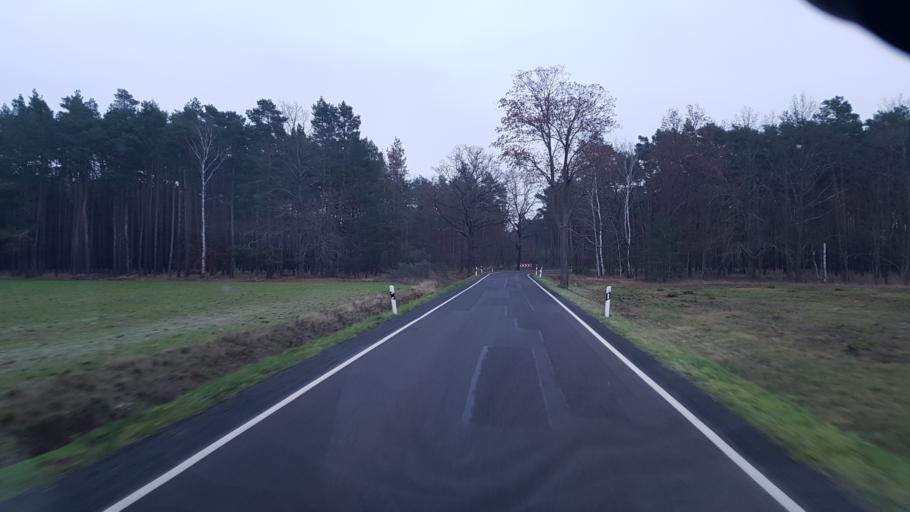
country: DE
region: Brandenburg
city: Drachhausen
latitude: 51.8909
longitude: 14.3441
